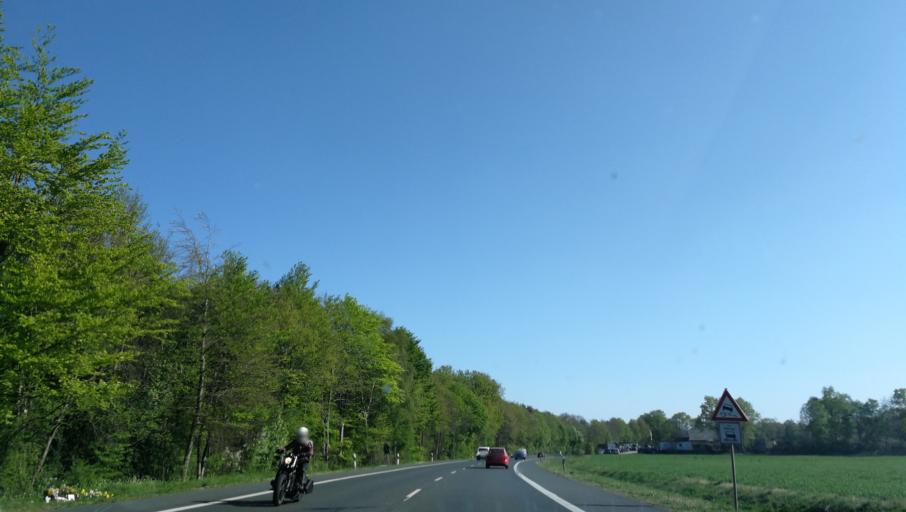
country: DE
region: North Rhine-Westphalia
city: Emsdetten
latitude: 52.2196
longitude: 7.5055
